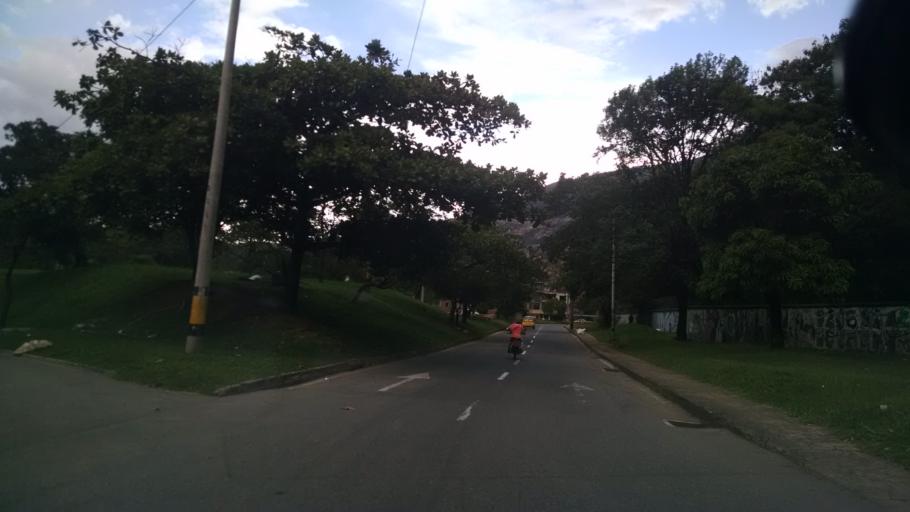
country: CO
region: Antioquia
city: Medellin
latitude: 6.2746
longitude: -75.5694
